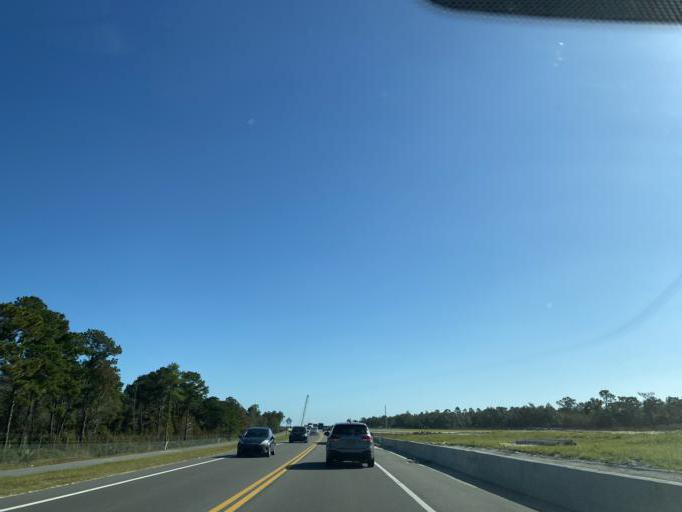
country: US
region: Florida
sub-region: Lake County
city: Mount Plymouth
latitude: 28.8126
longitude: -81.4618
